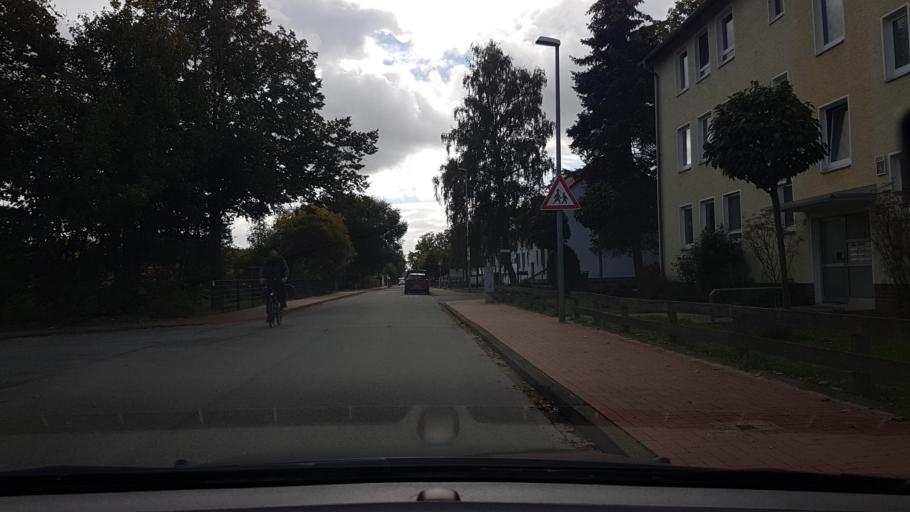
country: DE
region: Lower Saxony
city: Ronnenberg
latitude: 52.3382
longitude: 9.6718
